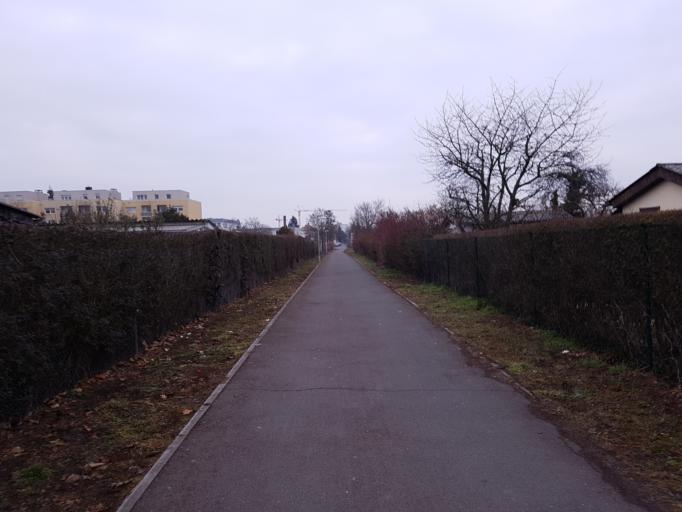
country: DE
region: Bavaria
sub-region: Regierungsbezirk Mittelfranken
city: Grossreuth bei Schweinau
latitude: 49.4471
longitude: 11.0320
